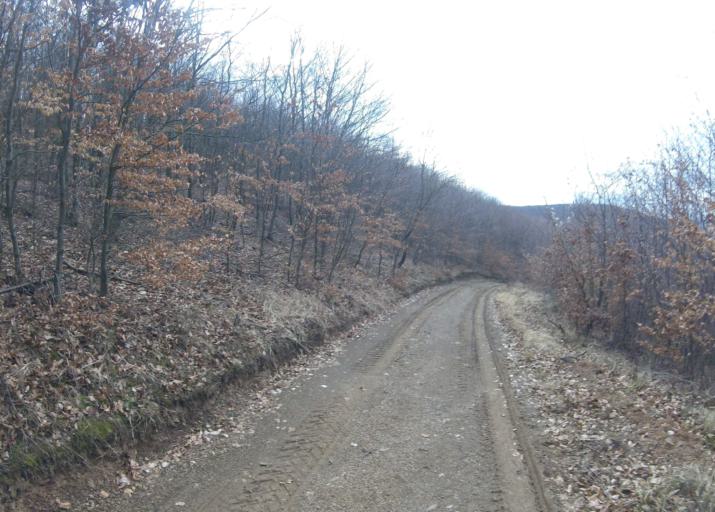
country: HU
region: Heves
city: Belapatfalva
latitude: 48.0312
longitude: 20.3620
